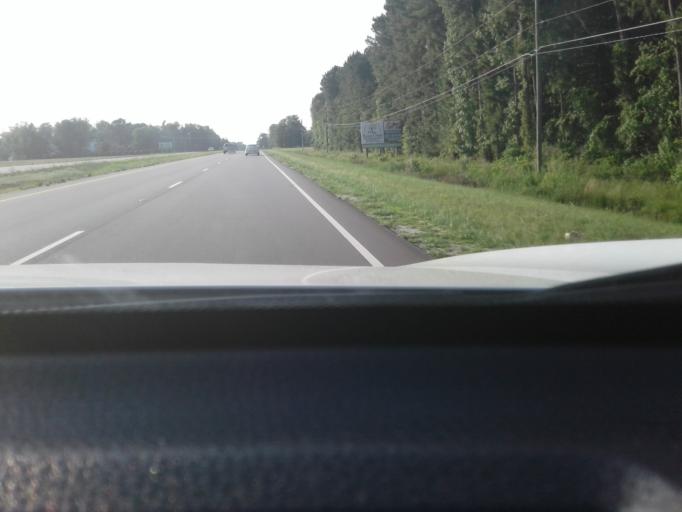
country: US
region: North Carolina
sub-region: Harnett County
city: Erwin
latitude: 35.3628
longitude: -78.7015
